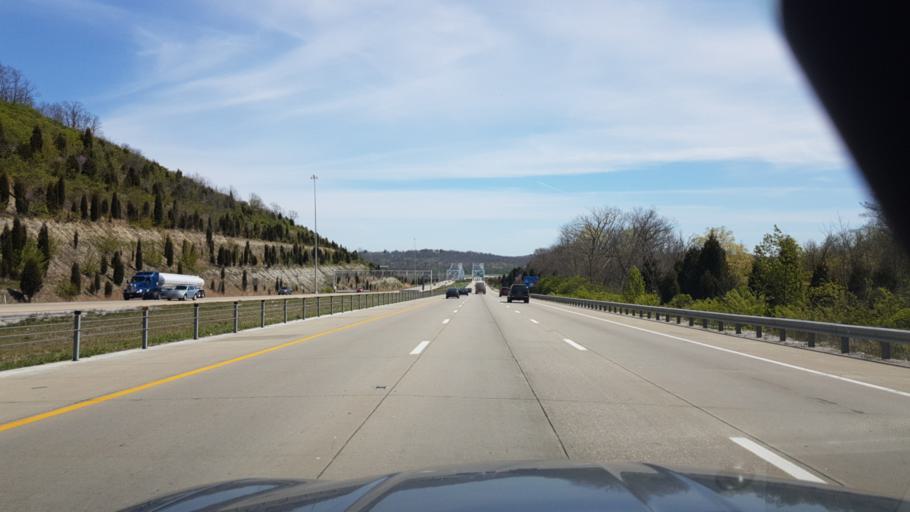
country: US
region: Kentucky
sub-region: Campbell County
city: Highland Heights
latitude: 39.0513
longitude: -84.4434
